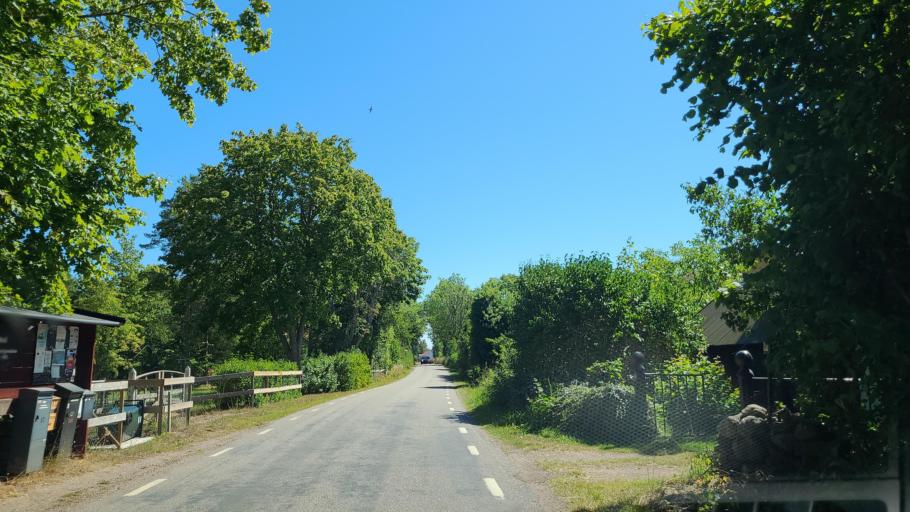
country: SE
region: Kalmar
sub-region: Borgholms Kommun
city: Borgholm
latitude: 56.7462
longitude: 16.6913
